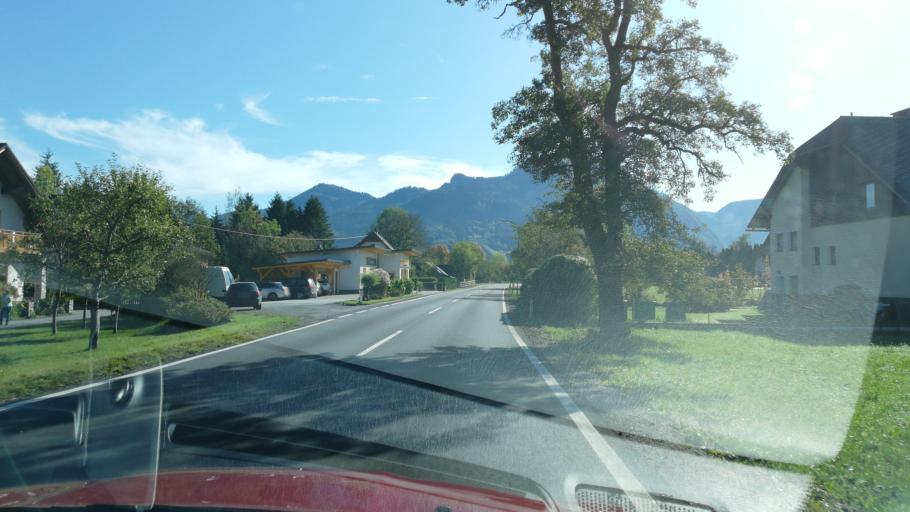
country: AT
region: Styria
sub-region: Politischer Bezirk Liezen
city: Landl
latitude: 47.6547
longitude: 14.7426
